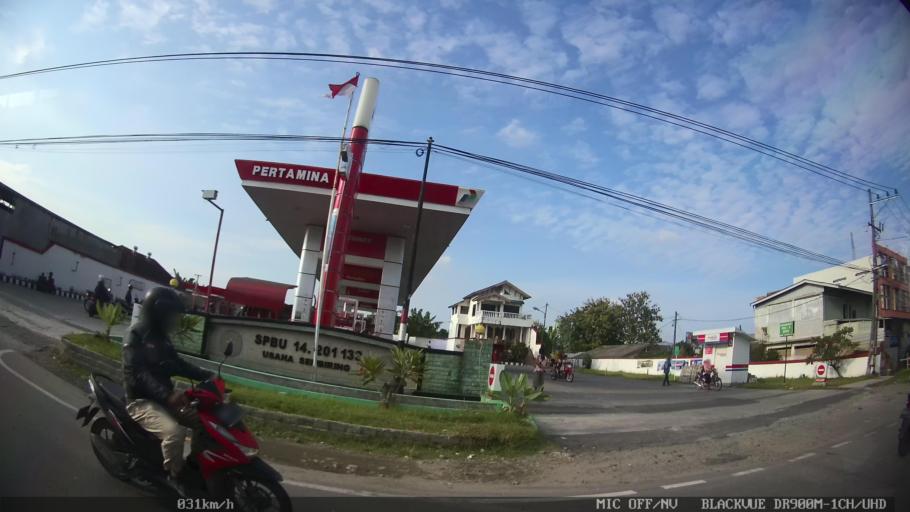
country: ID
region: North Sumatra
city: Medan
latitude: 3.6156
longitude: 98.6446
